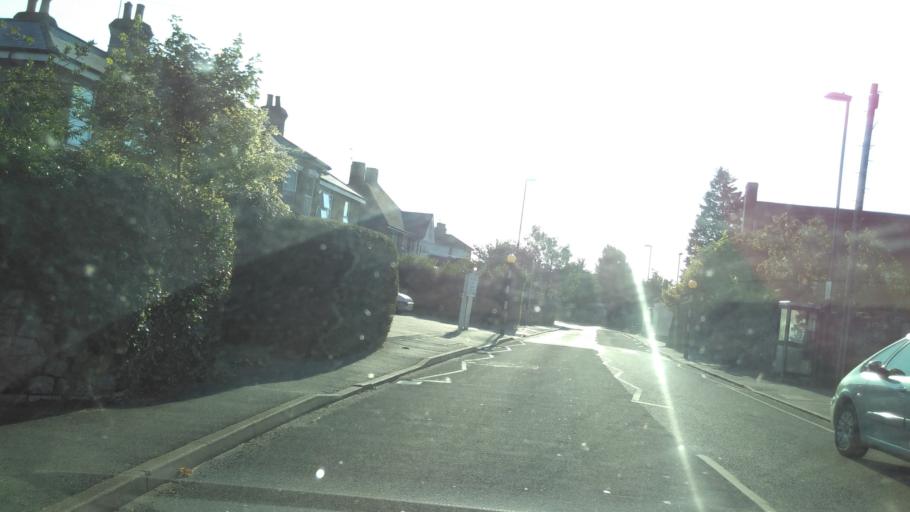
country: GB
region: England
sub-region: Kent
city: Whitstable
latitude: 51.3505
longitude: 1.0207
